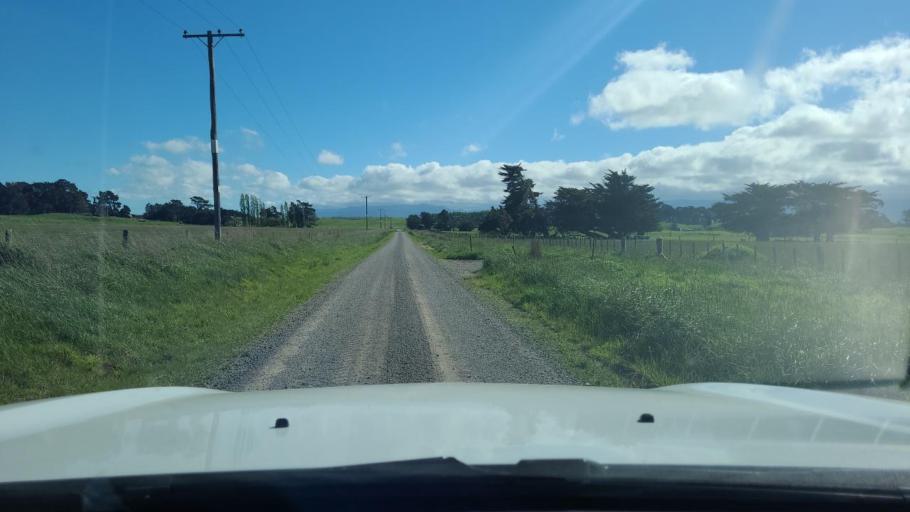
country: NZ
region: Wellington
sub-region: South Wairarapa District
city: Waipawa
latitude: -41.2000
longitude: 175.3615
